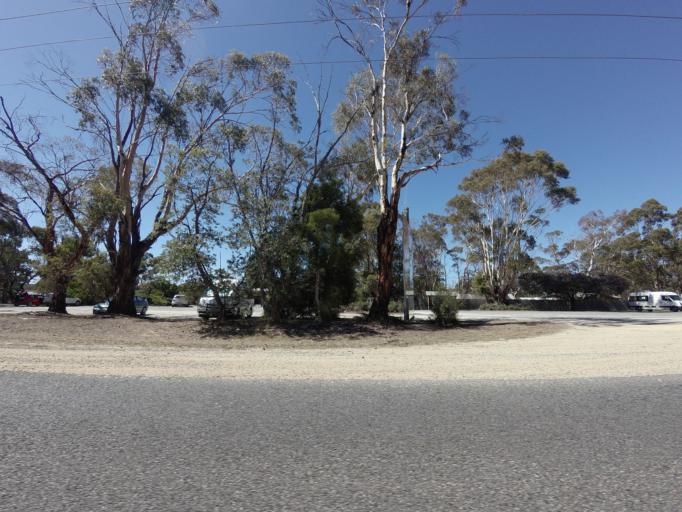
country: AU
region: Tasmania
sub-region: Break O'Day
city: St Helens
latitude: -41.8375
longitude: 148.2552
